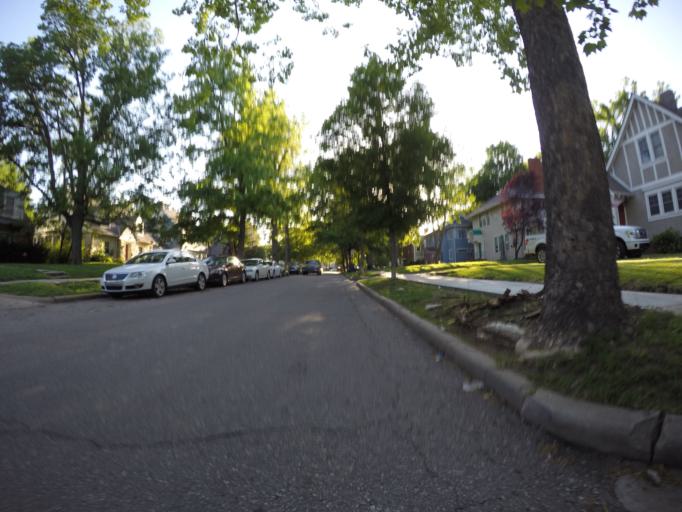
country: US
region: Kansas
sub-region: Riley County
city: Manhattan
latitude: 39.1851
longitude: -96.5858
